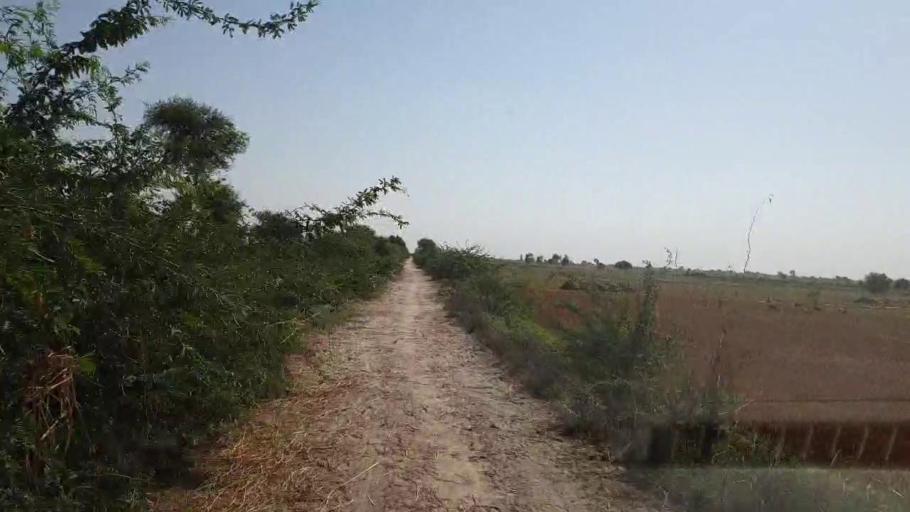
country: PK
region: Sindh
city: Kadhan
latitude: 24.6235
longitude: 68.9954
